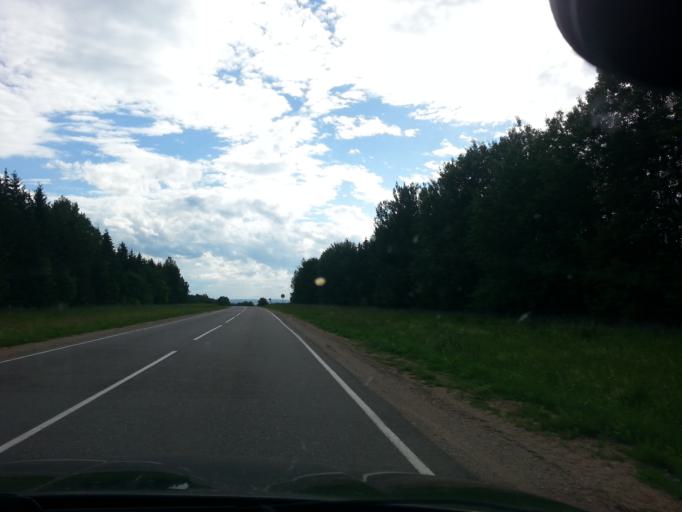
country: BY
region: Grodnenskaya
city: Astravyets
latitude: 54.7881
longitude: 26.0751
